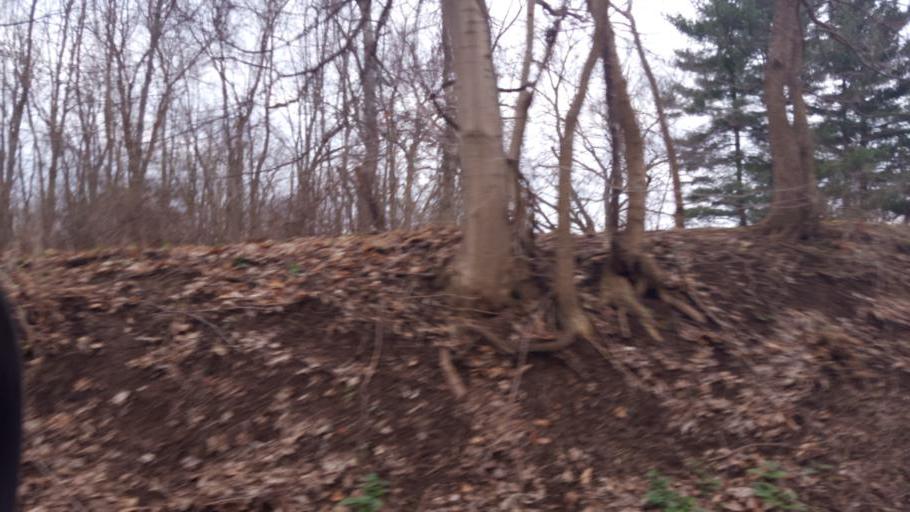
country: US
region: Ohio
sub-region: Ashland County
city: Loudonville
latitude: 40.7193
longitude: -82.3477
